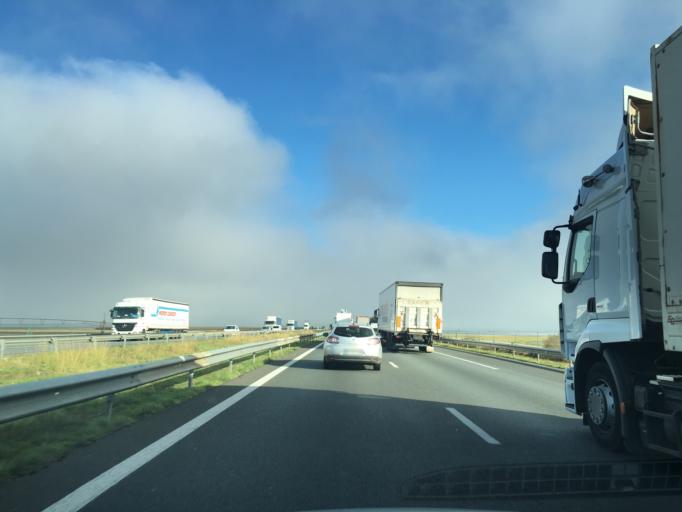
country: FR
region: Aquitaine
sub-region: Departement de la Gironde
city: Marcheprime
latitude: 44.6806
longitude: -0.7910
